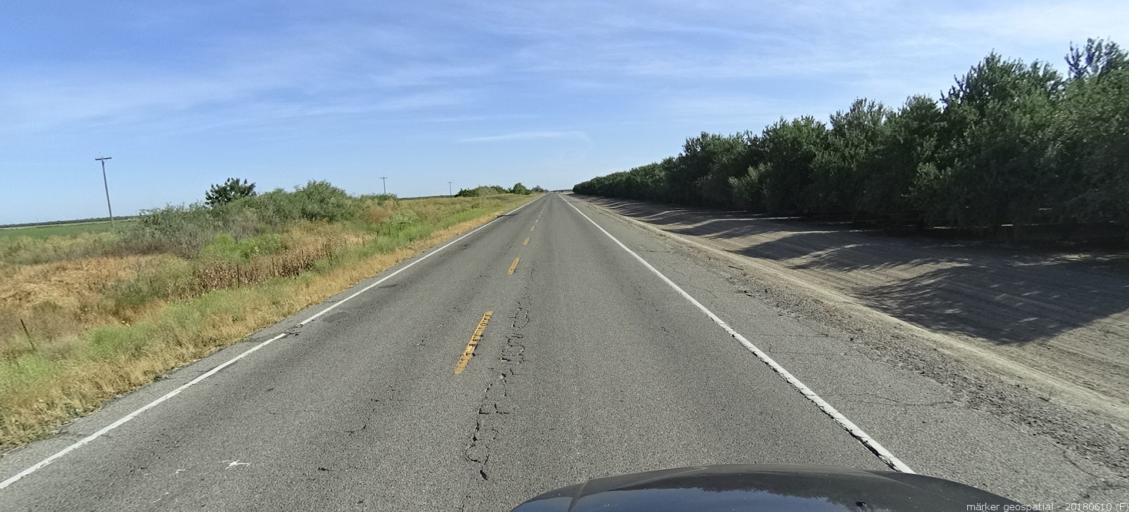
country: US
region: California
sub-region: Madera County
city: Fairmead
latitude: 36.9775
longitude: -120.2560
